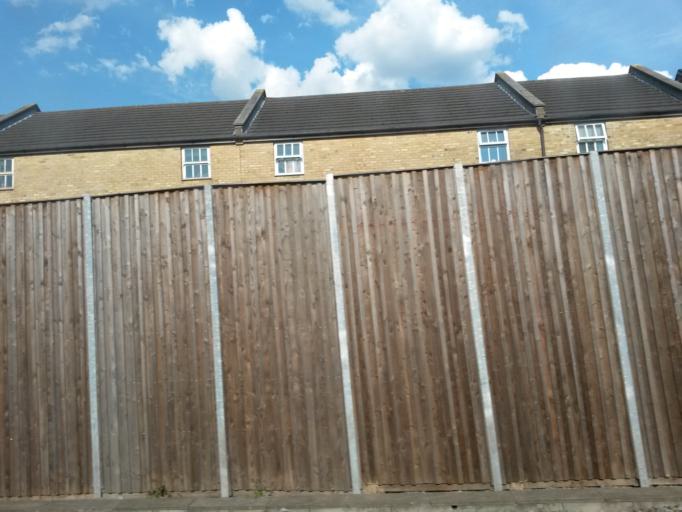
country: GB
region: England
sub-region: Greater London
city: Poplar
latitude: 51.4864
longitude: -0.0438
